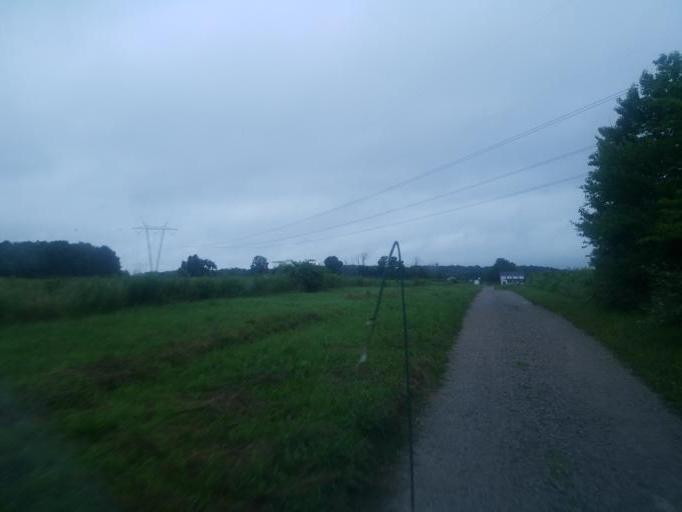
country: US
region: Ohio
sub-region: Richland County
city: Lexington
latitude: 40.5946
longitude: -82.6661
